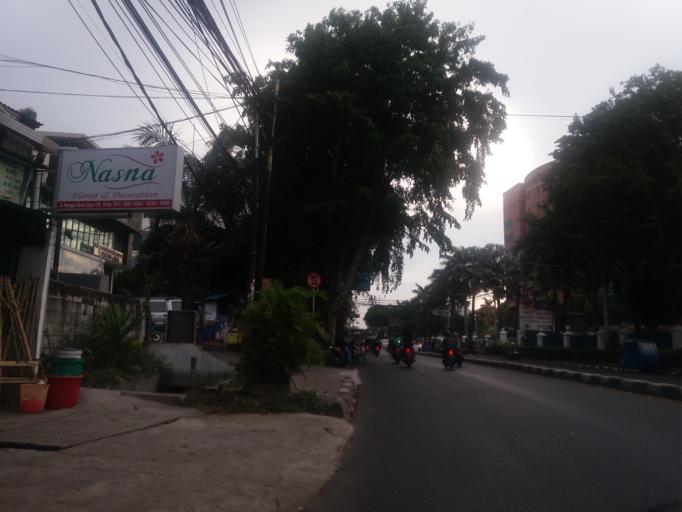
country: ID
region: Jakarta Raya
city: Jakarta
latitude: -6.1479
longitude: 106.8306
